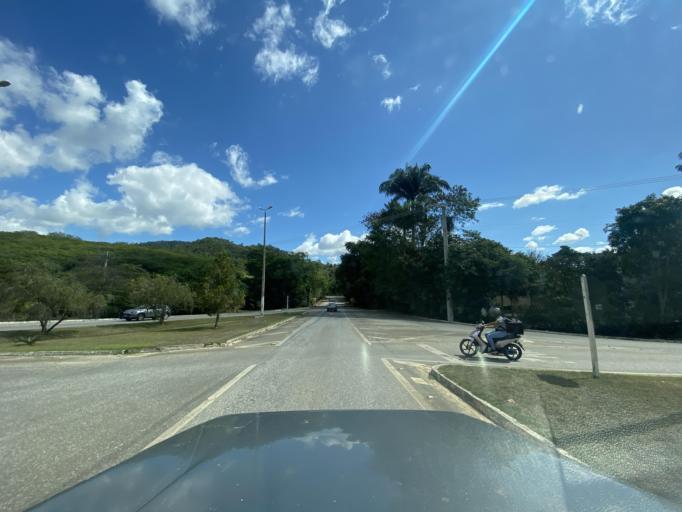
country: BR
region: Espirito Santo
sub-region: Jeronimo Monteiro
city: Jeronimo Monteiro
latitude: -20.7611
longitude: -41.4573
